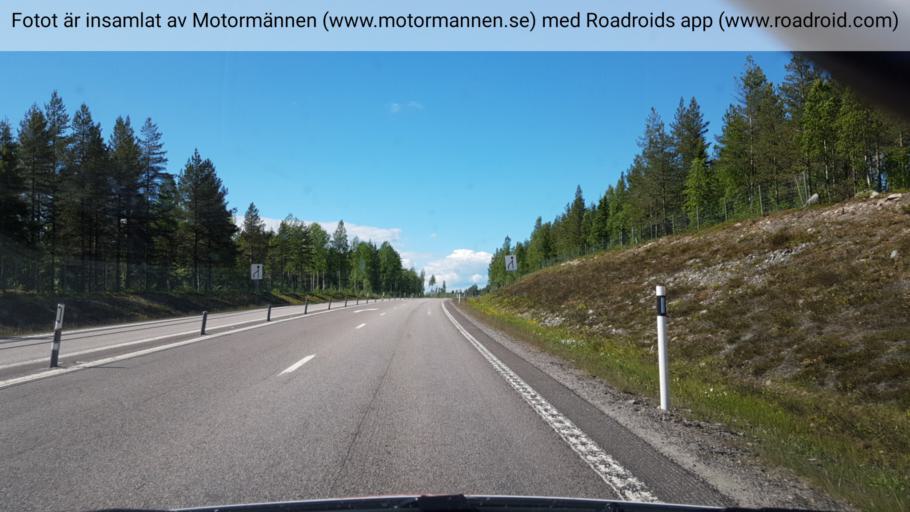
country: SE
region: Norrbotten
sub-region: Kalix Kommun
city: Toere
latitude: 65.9051
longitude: 22.8449
